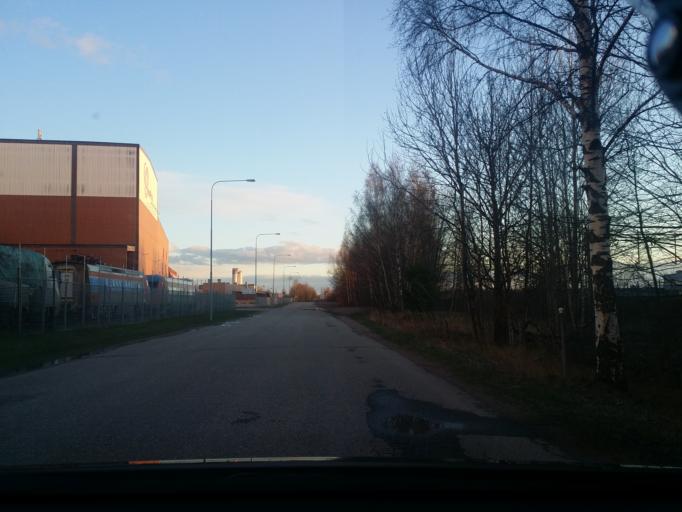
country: SE
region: Vaestmanland
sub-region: Vasteras
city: Hokasen
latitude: 59.6388
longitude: 16.5773
